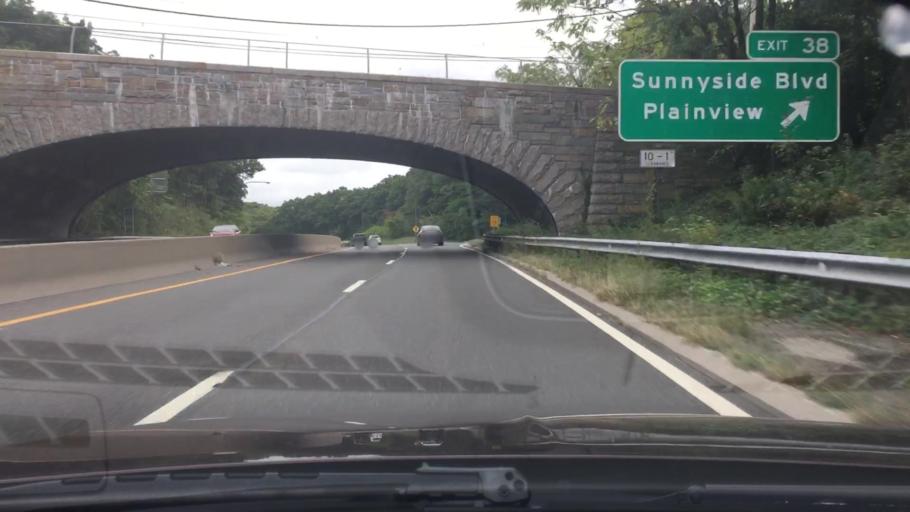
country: US
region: New York
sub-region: Nassau County
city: Plainview
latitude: 40.7989
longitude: -73.4684
